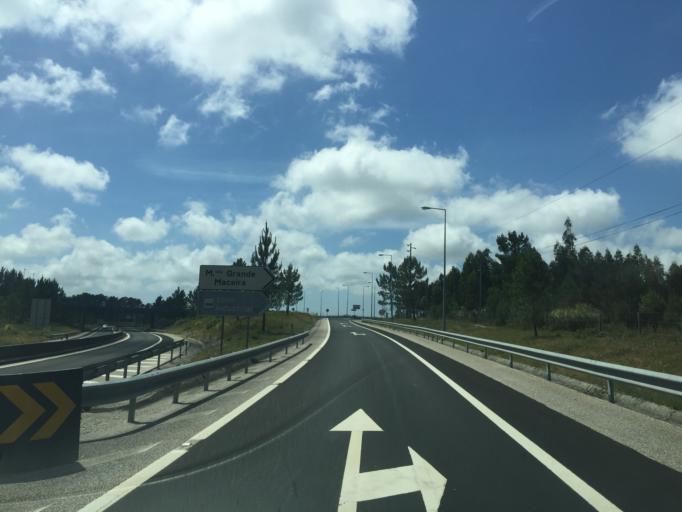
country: PT
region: Leiria
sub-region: Marinha Grande
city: Marinha Grande
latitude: 39.7153
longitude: -8.9220
